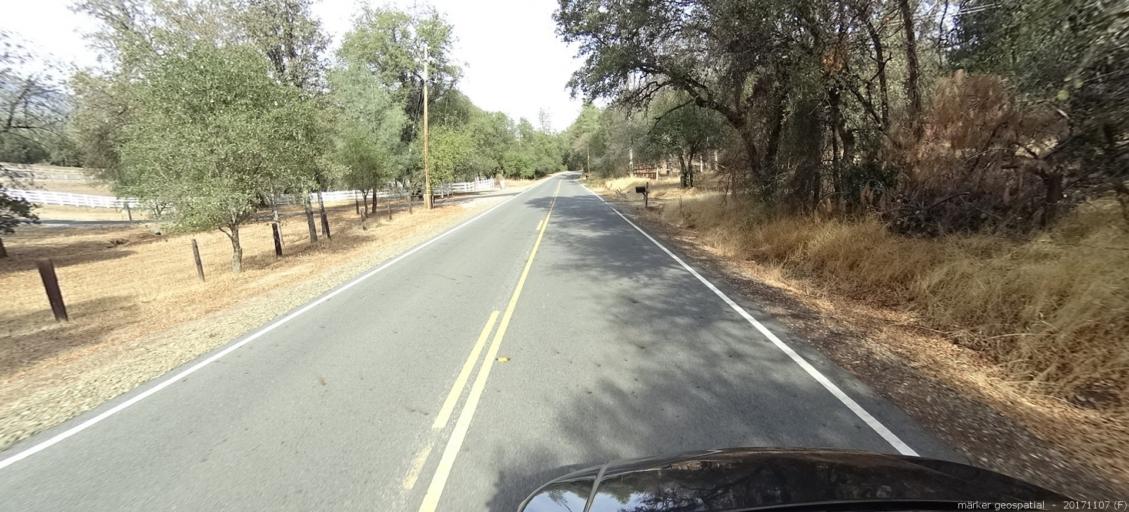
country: US
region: California
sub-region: Shasta County
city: Shasta
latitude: 40.4919
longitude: -122.5488
